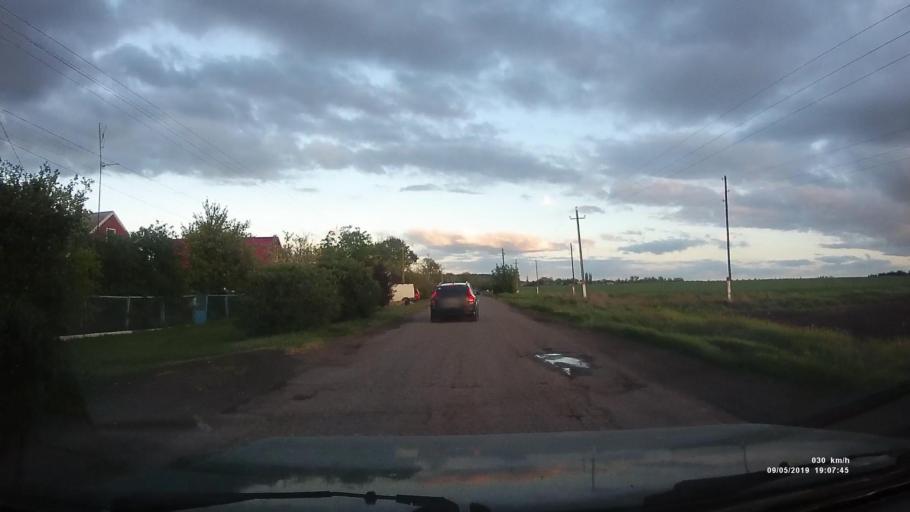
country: RU
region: Krasnodarskiy
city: Kanelovskaya
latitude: 46.7330
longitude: 39.1987
